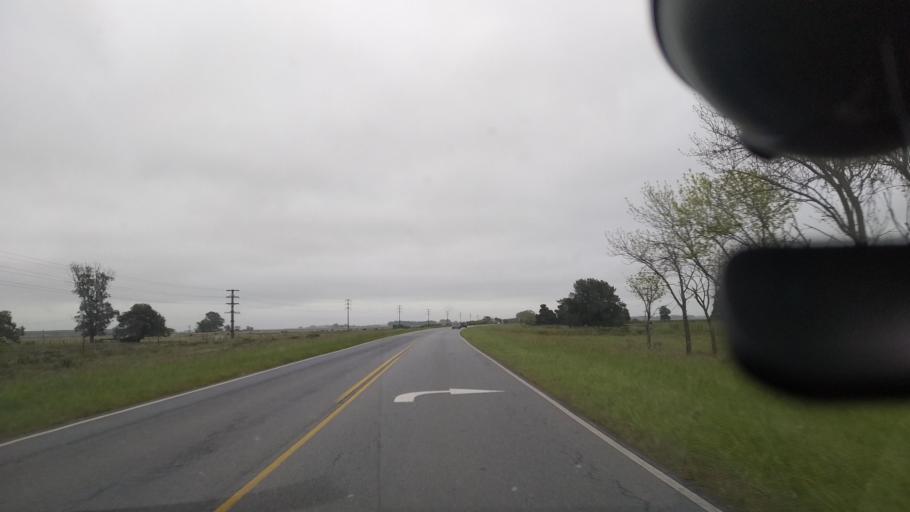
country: AR
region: Buenos Aires
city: Veronica
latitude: -35.3700
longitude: -57.3871
